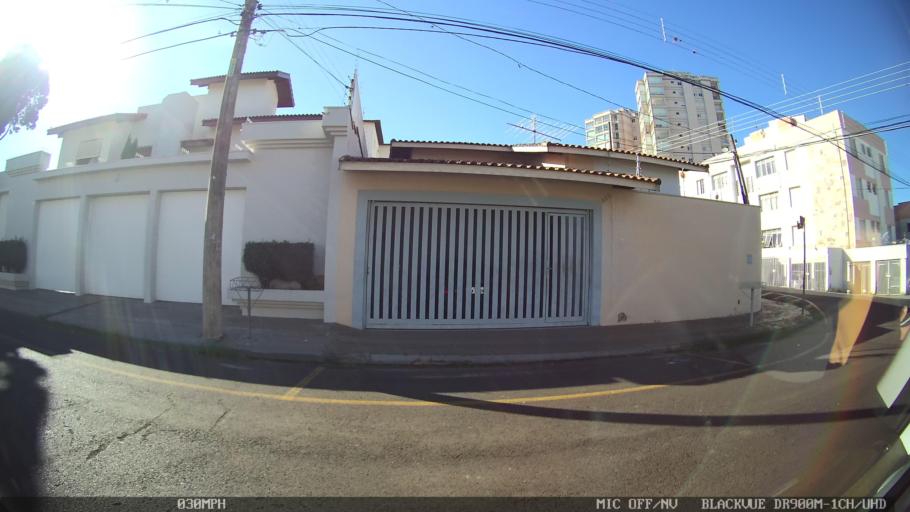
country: BR
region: Sao Paulo
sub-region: Franca
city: Franca
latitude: -20.5461
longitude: -47.4061
